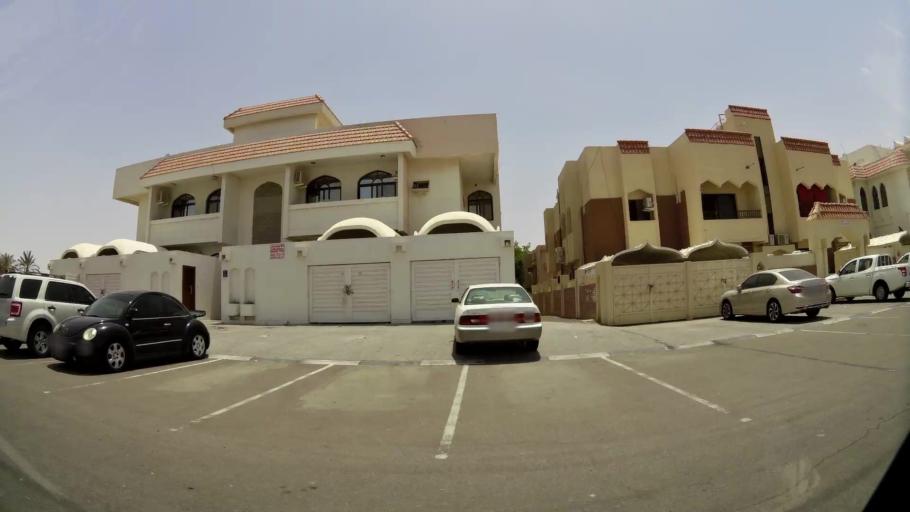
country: AE
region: Abu Dhabi
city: Al Ain
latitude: 24.2075
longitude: 55.7259
